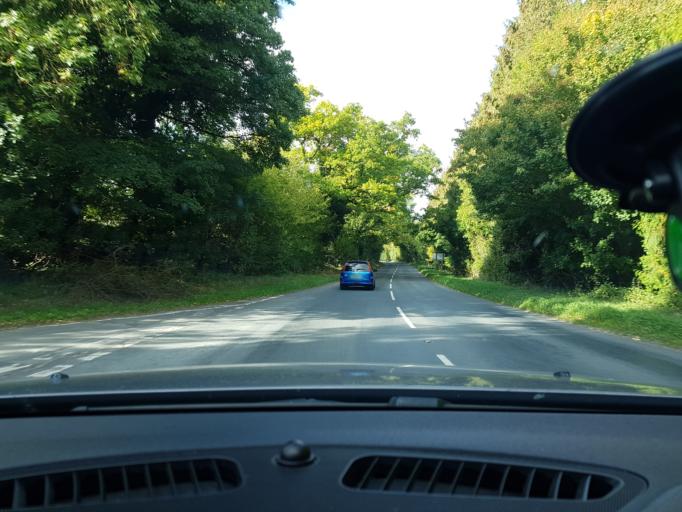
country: GB
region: England
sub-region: Wiltshire
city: Ramsbury
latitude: 51.4608
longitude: -1.6000
